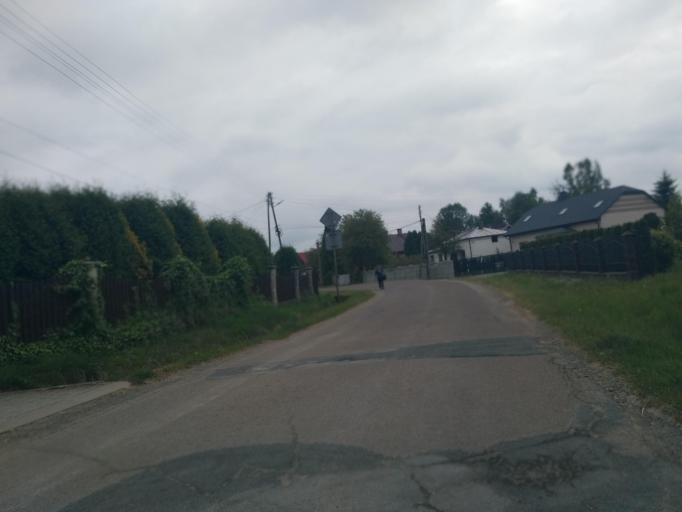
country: PL
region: Subcarpathian Voivodeship
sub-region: Powiat krosnienski
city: Chorkowka
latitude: 49.6647
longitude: 21.7162
